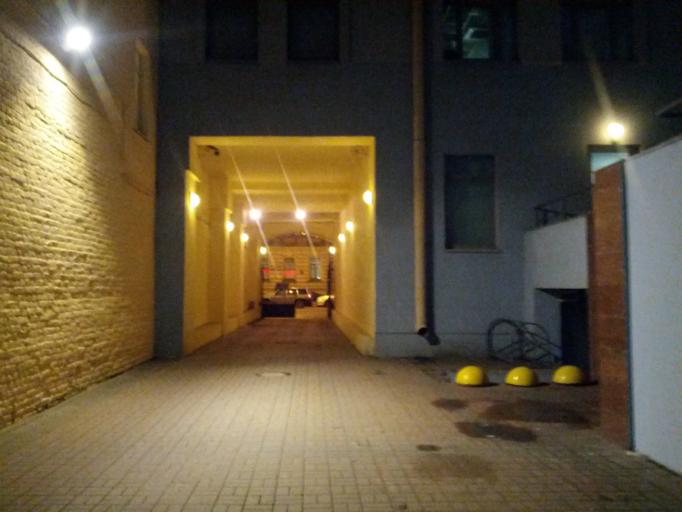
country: RU
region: St.-Petersburg
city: Centralniy
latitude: 59.9316
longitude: 30.3680
